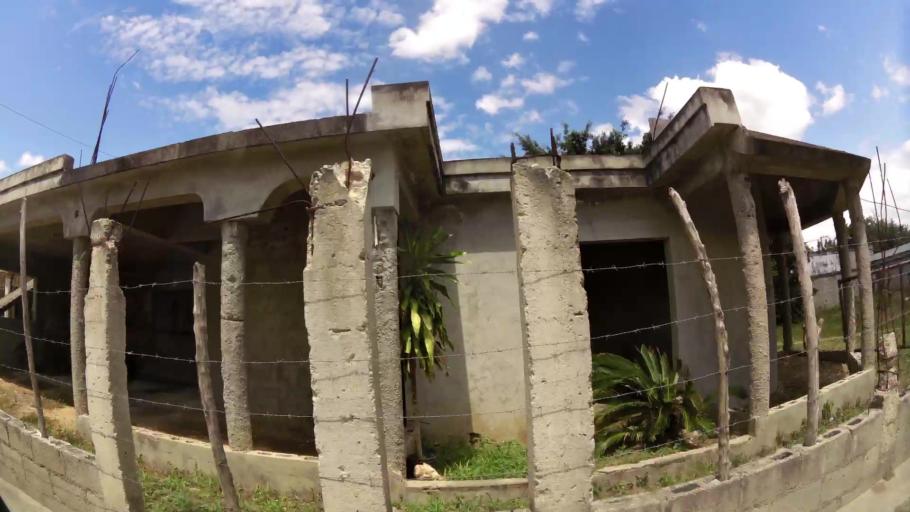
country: DO
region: San Cristobal
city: San Cristobal
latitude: 18.4096
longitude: -70.1018
